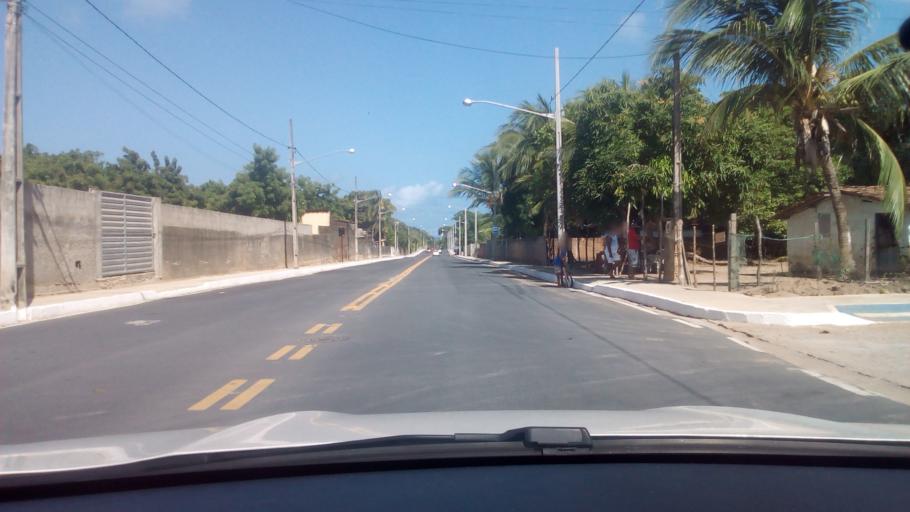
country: BR
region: Paraiba
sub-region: Joao Pessoa
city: Joao Pessoa
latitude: -7.1501
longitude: -34.8035
